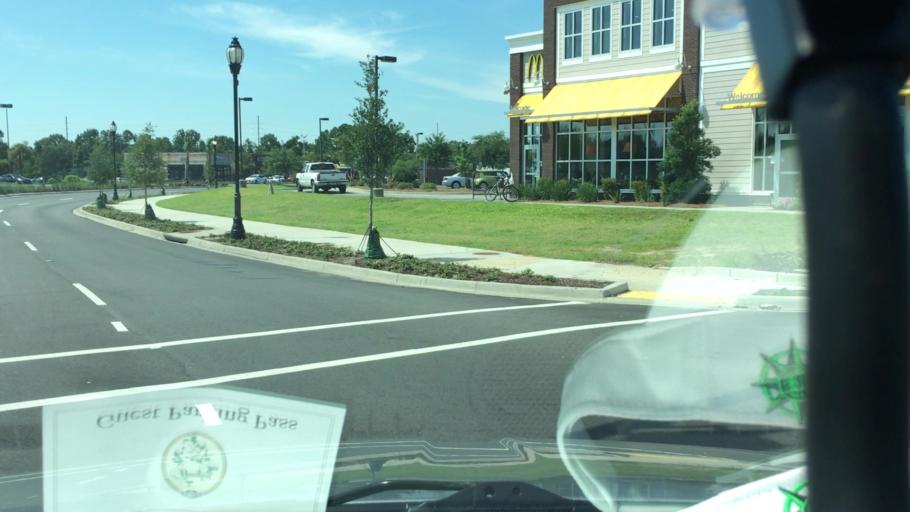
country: US
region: South Carolina
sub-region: Beaufort County
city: Burton
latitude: 32.4404
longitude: -80.7053
